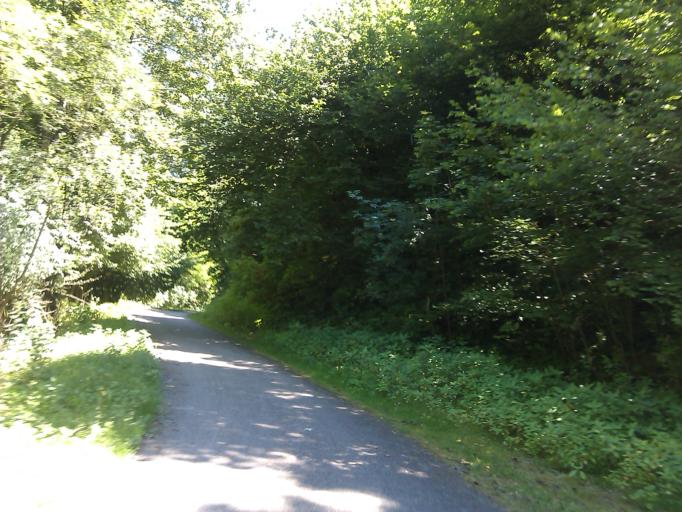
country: IT
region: Veneto
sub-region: Provincia di Vicenza
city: Enego
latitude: 45.9540
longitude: 11.7163
